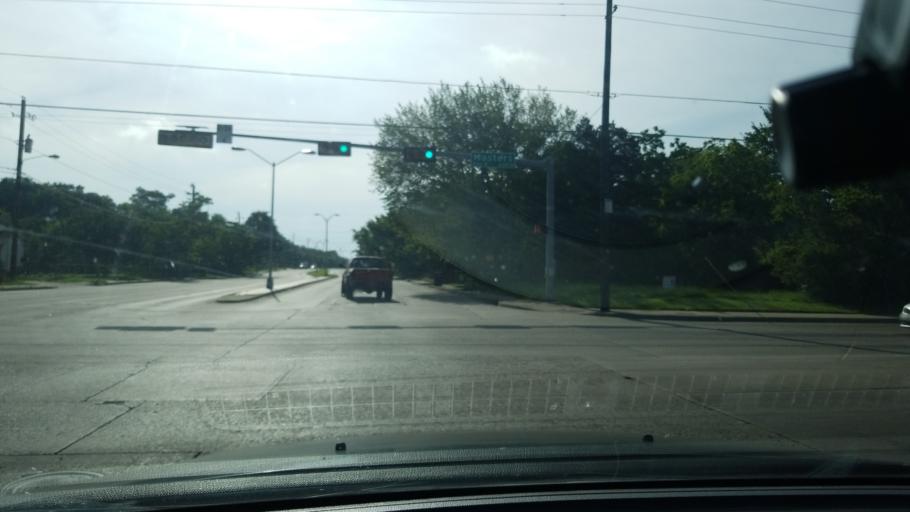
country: US
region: Texas
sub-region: Dallas County
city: Balch Springs
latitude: 32.7194
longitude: -96.6485
